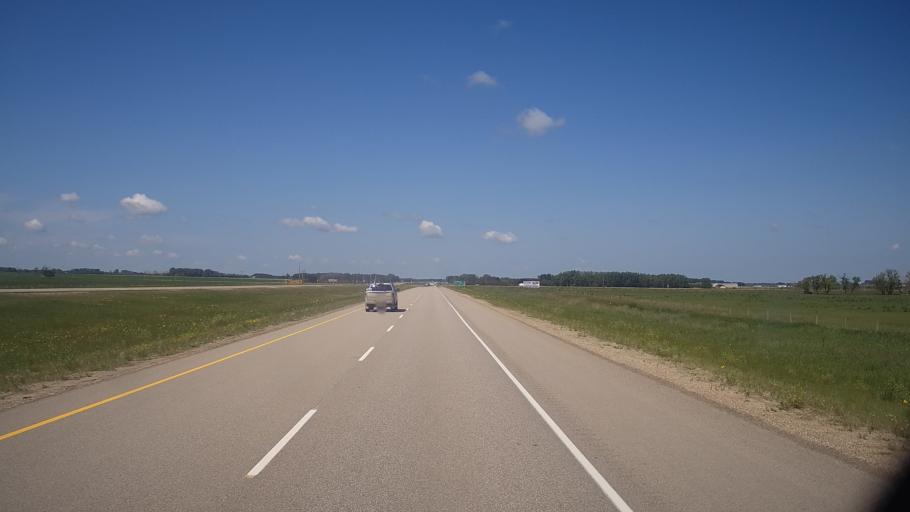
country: CA
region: Saskatchewan
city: Saskatoon
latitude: 52.0123
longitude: -106.3742
